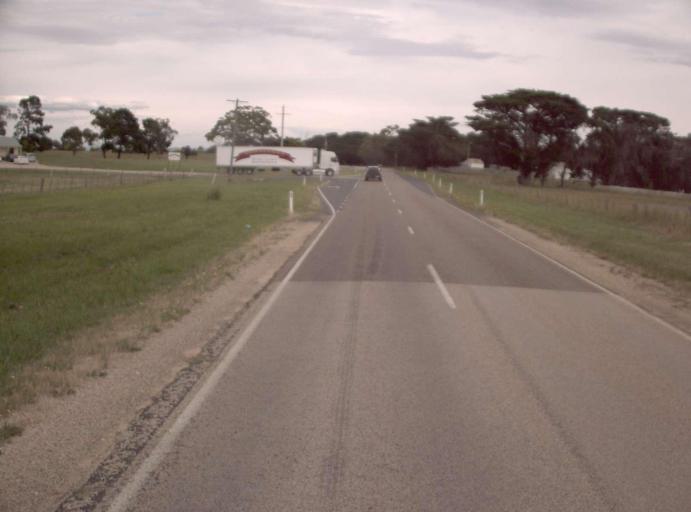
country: AU
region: Victoria
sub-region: East Gippsland
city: Bairnsdale
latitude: -37.8117
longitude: 147.4869
